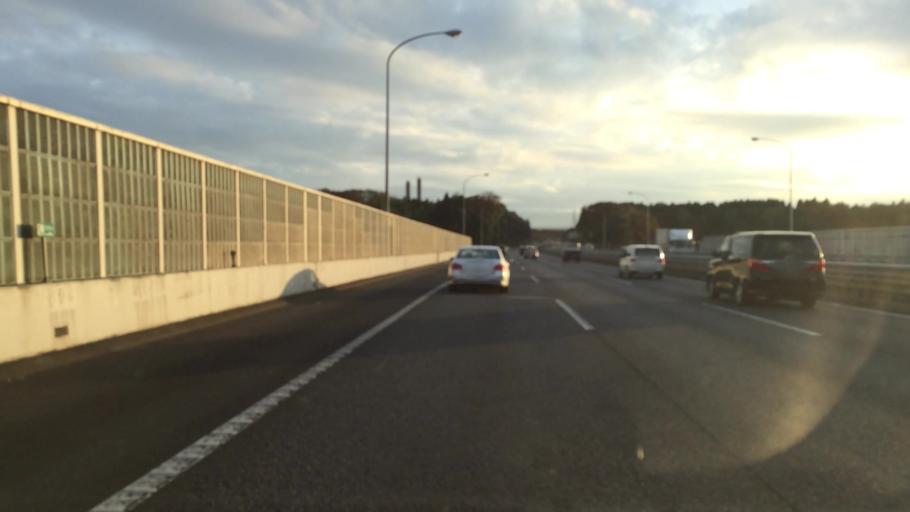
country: JP
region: Chiba
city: Shisui
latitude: 35.7192
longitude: 140.2897
